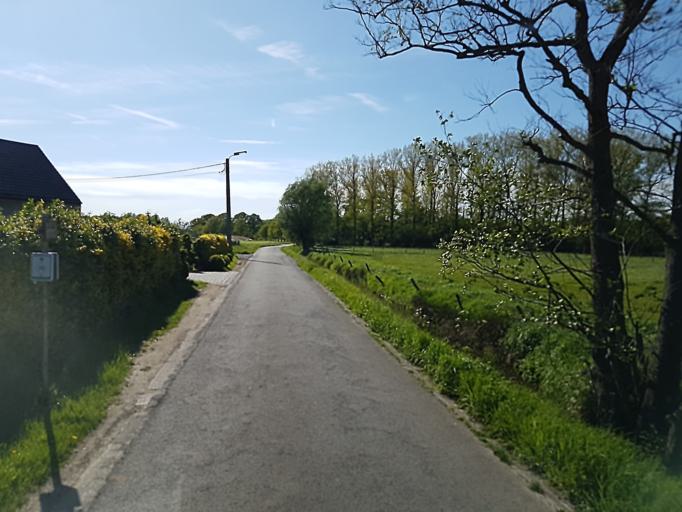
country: BE
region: Flanders
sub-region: Provincie Vlaams-Brabant
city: Boortmeerbeek
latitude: 51.0056
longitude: 4.5760
